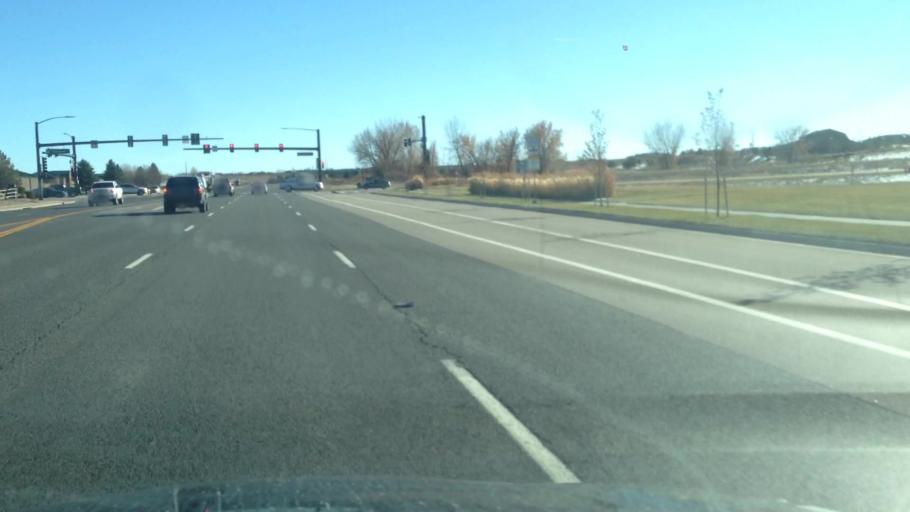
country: US
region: Colorado
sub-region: Douglas County
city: Stonegate
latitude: 39.5554
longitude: -104.7950
